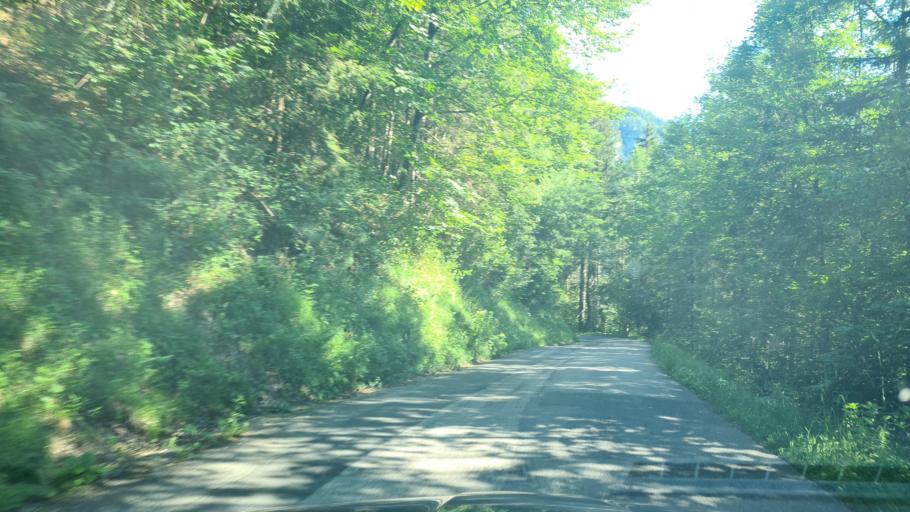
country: AT
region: Salzburg
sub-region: Politischer Bezirk Zell am See
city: Unken
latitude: 47.6495
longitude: 12.7122
